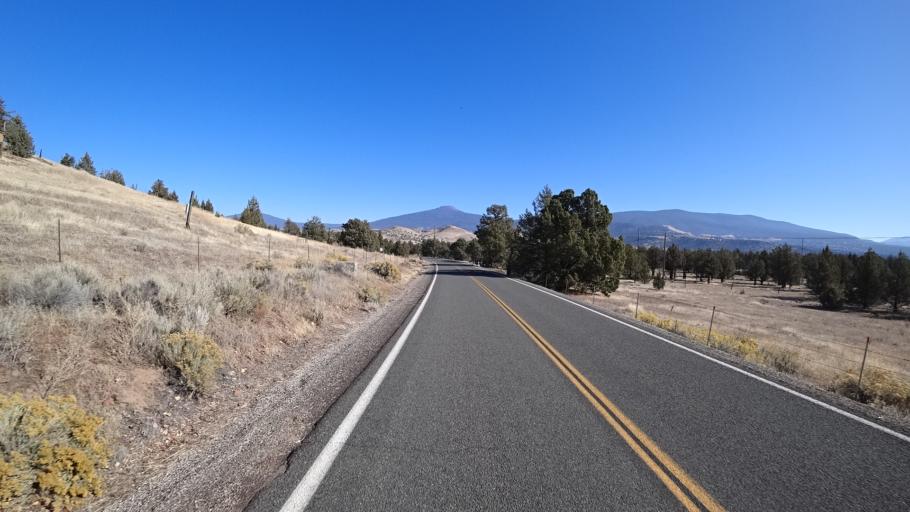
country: US
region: California
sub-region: Siskiyou County
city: Montague
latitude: 41.6591
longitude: -122.3710
